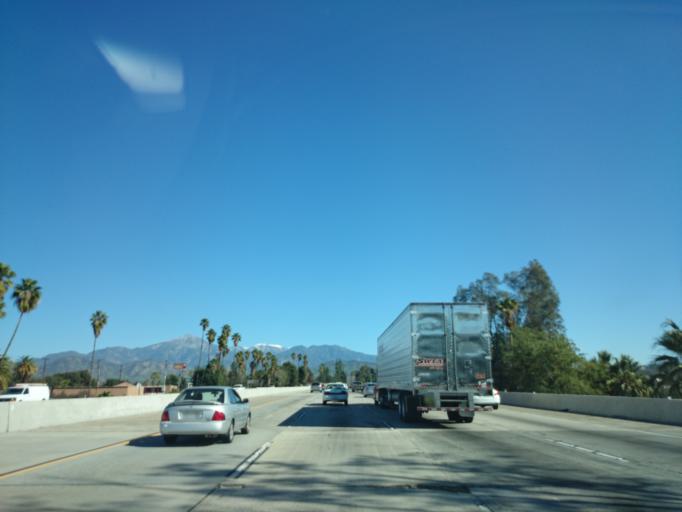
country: US
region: California
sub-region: San Bernardino County
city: Redlands
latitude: 34.0617
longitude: -117.1830
